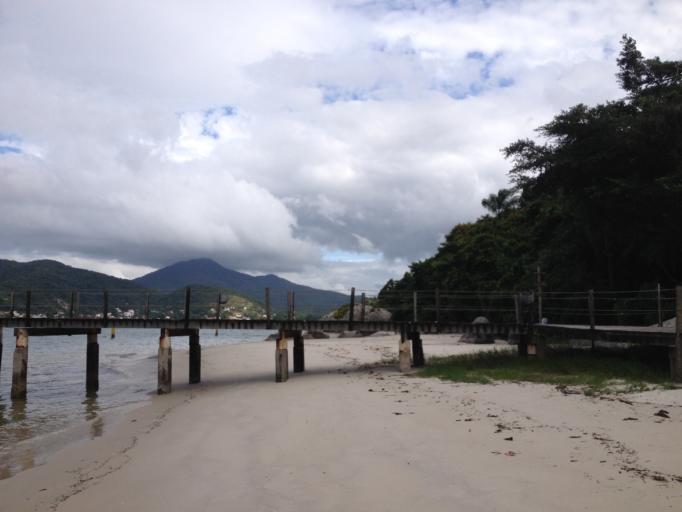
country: BR
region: Santa Catarina
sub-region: Porto Belo
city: Porto Belo
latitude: -27.1435
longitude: -48.5445
